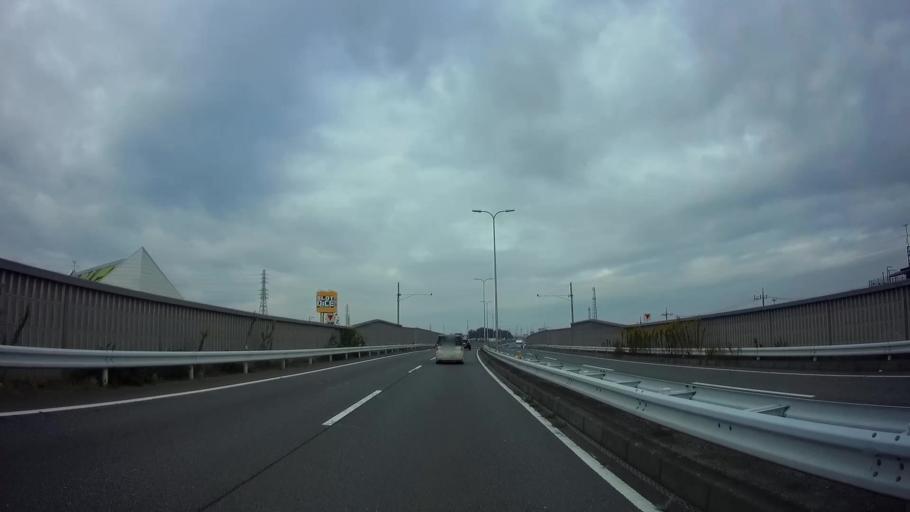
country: JP
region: Saitama
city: Kumagaya
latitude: 36.1670
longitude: 139.3822
